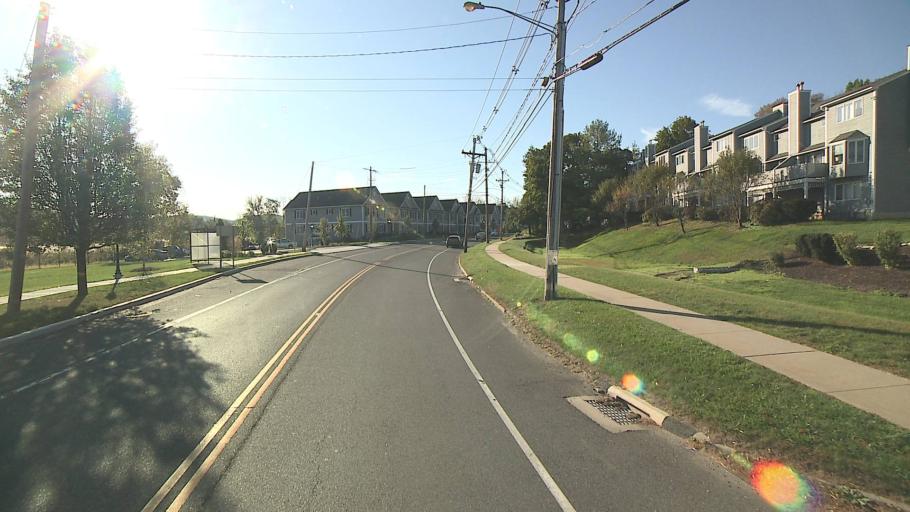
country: US
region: Connecticut
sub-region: Fairfield County
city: Bethel
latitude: 41.3829
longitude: -73.4250
